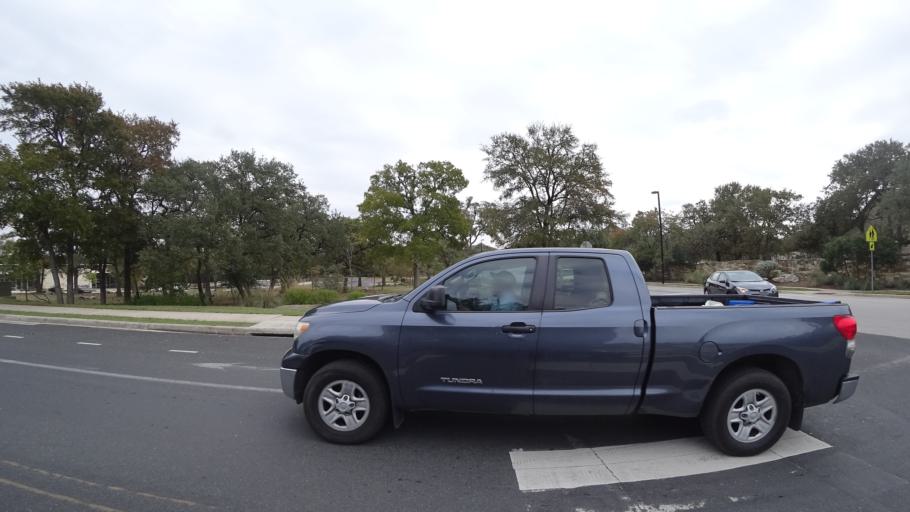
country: US
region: Texas
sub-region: Travis County
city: Shady Hollow
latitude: 30.1927
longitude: -97.9096
